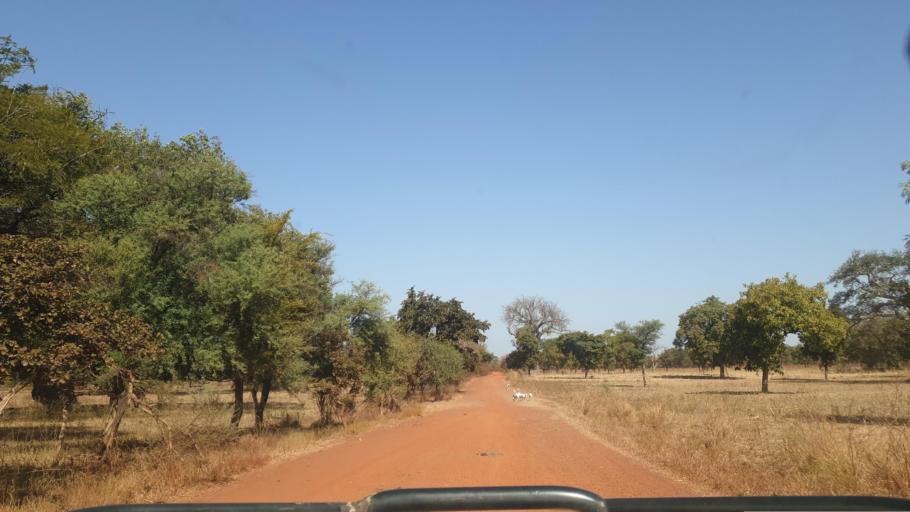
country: ML
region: Sikasso
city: Bougouni
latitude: 11.8430
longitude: -6.9782
